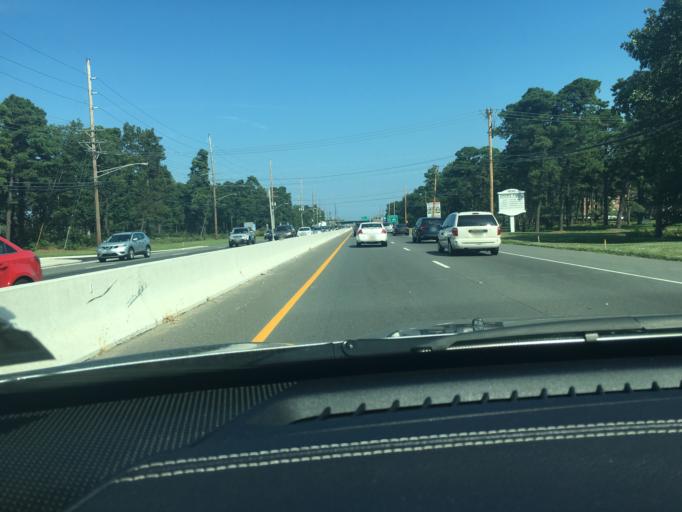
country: US
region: New Jersey
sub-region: Ocean County
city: Leisure Village
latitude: 40.0531
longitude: -74.1784
